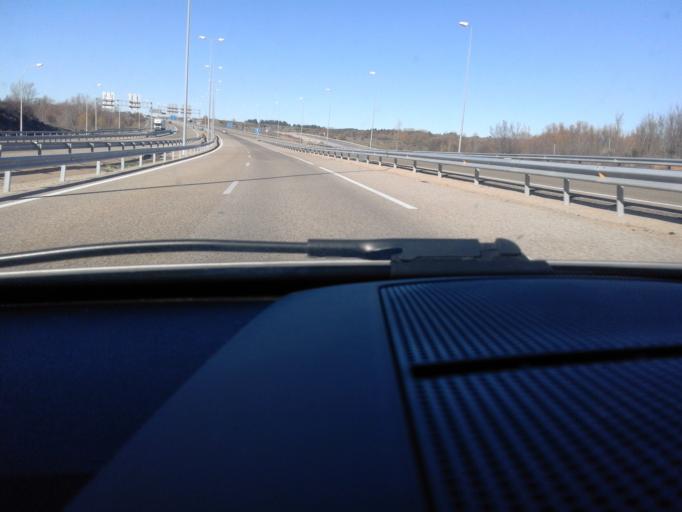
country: ES
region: Castille and Leon
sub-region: Provincia de Leon
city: Valverde de la Virgen
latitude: 42.5768
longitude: -5.6647
